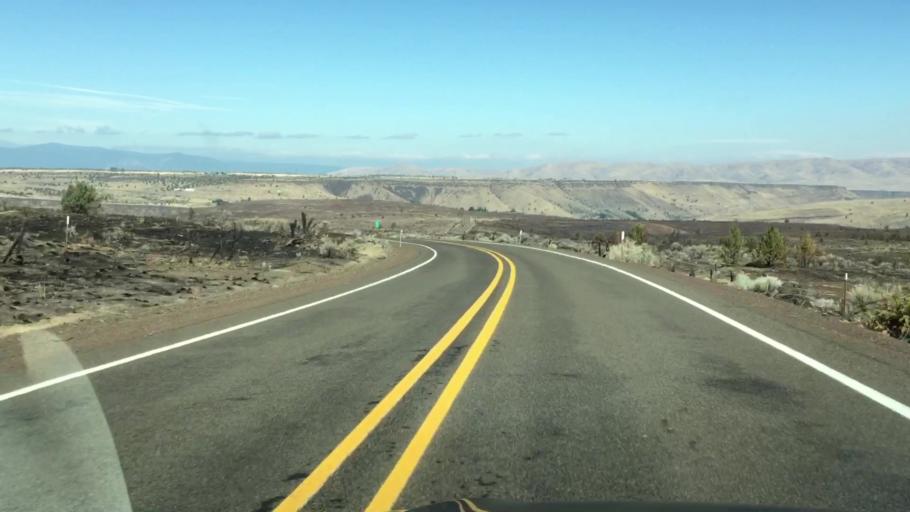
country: US
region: Oregon
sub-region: Jefferson County
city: Warm Springs
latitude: 45.1483
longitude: -121.0591
